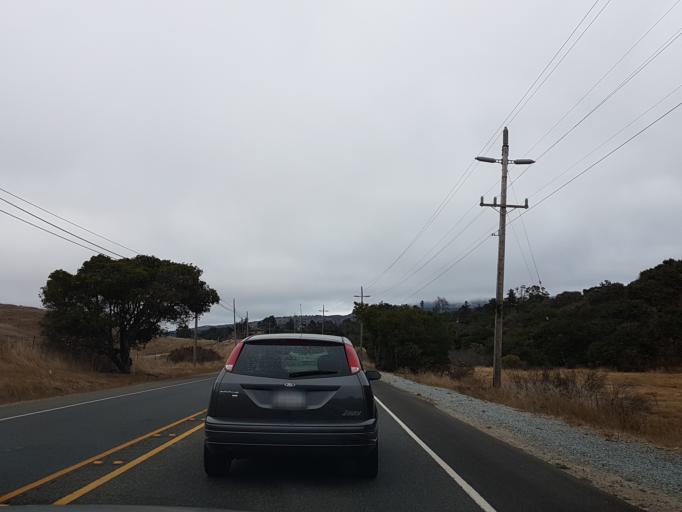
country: US
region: California
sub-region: Monterey County
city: Carmel Valley Village
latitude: 36.5724
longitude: -121.7406
